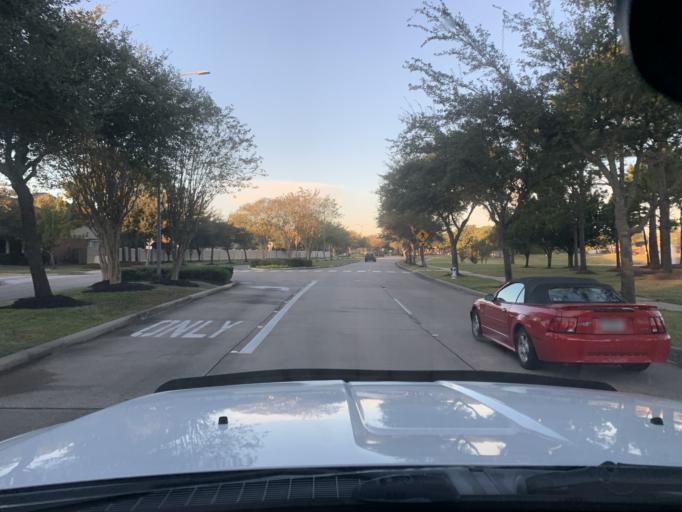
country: US
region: Texas
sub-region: Fort Bend County
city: Four Corners
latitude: 29.6501
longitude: -95.6357
